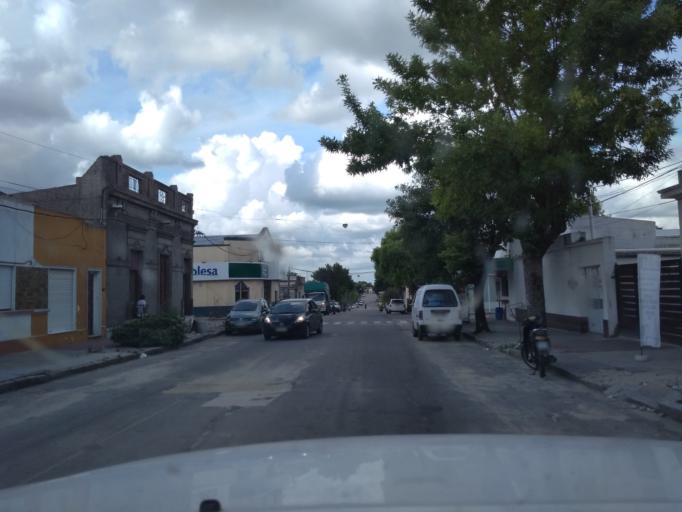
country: UY
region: Florida
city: Florida
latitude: -34.0928
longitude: -56.2182
